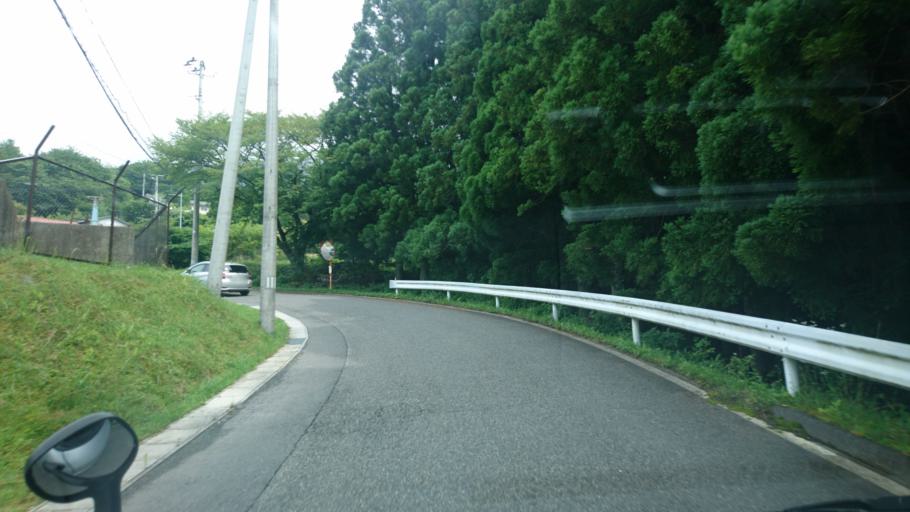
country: JP
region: Iwate
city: Ofunato
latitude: 39.1346
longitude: 141.7844
